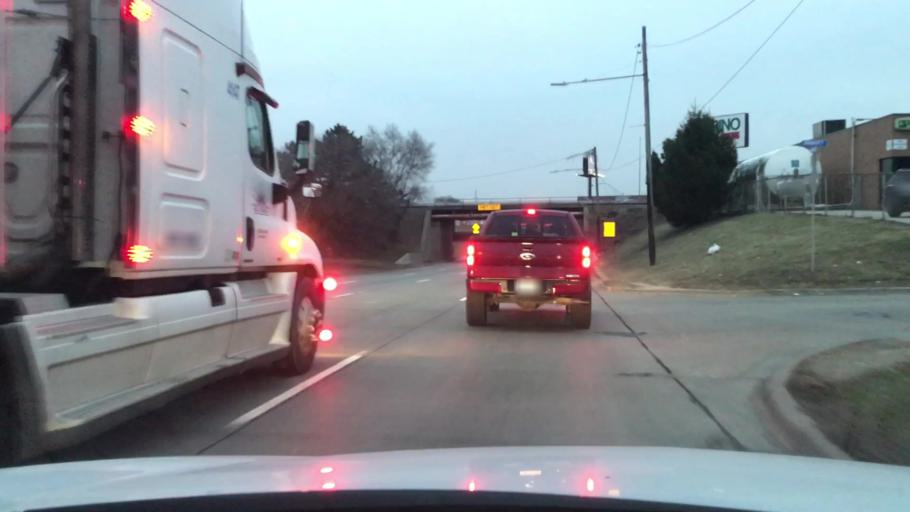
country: US
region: Michigan
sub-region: Wayne County
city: Lincoln Park
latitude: 42.2531
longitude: -83.1875
